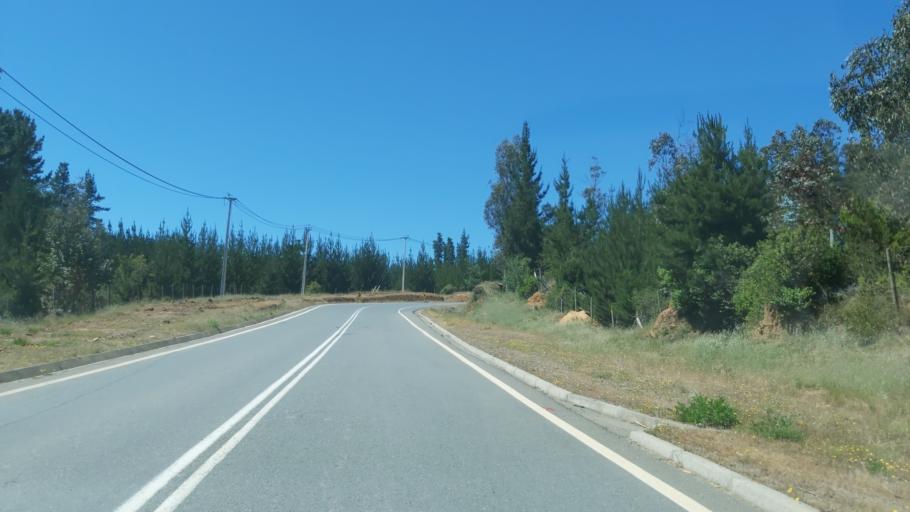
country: CL
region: Maule
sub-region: Provincia de Talca
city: Talca
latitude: -34.9574
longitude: -71.9612
